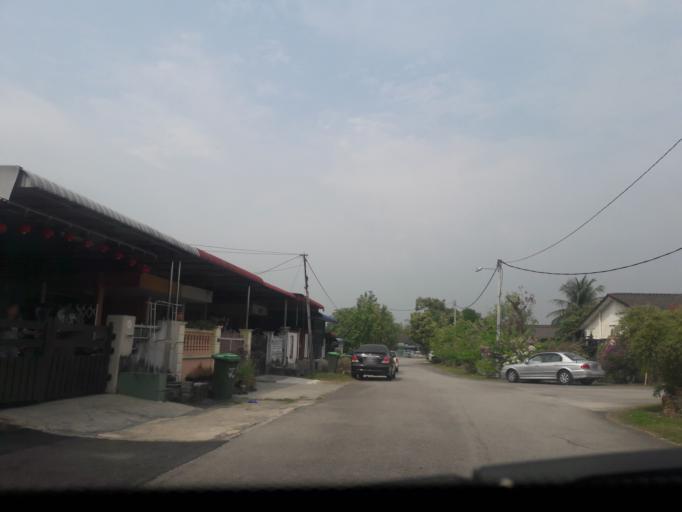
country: MY
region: Kedah
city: Kulim
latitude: 5.3585
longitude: 100.5418
